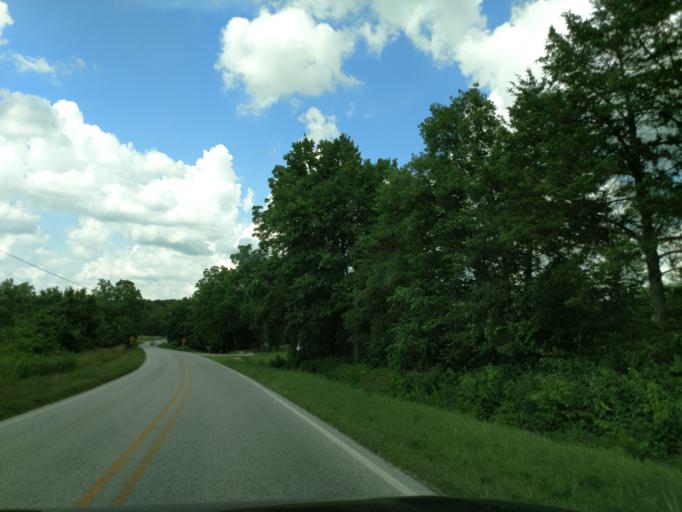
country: US
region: Arkansas
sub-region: Carroll County
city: Berryville
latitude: 36.4161
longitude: -93.5600
